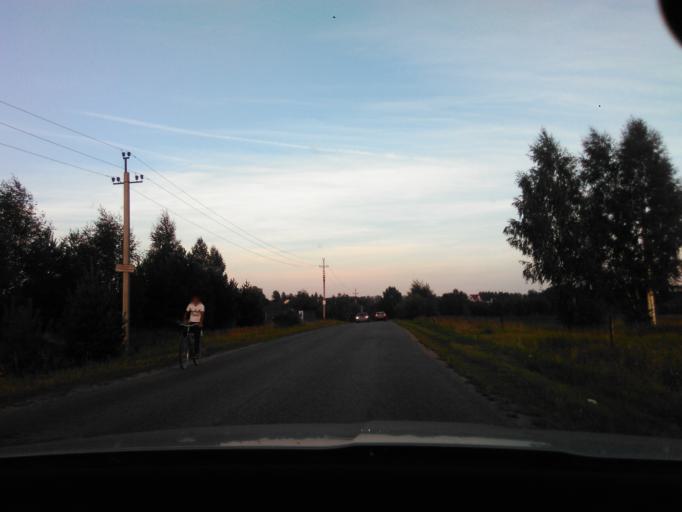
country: RU
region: Tverskaya
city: Zavidovo
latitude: 56.6079
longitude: 36.6085
